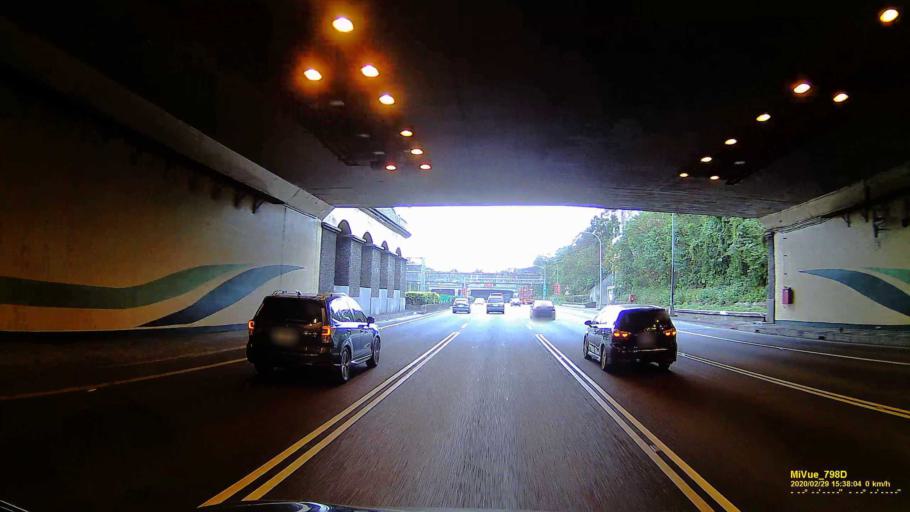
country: TW
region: Taiwan
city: Daxi
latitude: 24.9063
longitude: 121.2842
